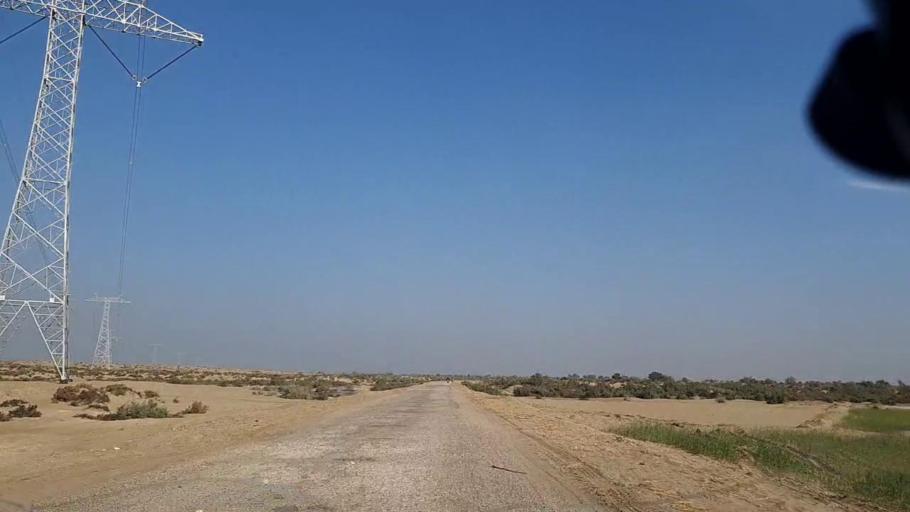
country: PK
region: Sindh
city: Khanpur
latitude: 27.6858
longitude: 69.4668
